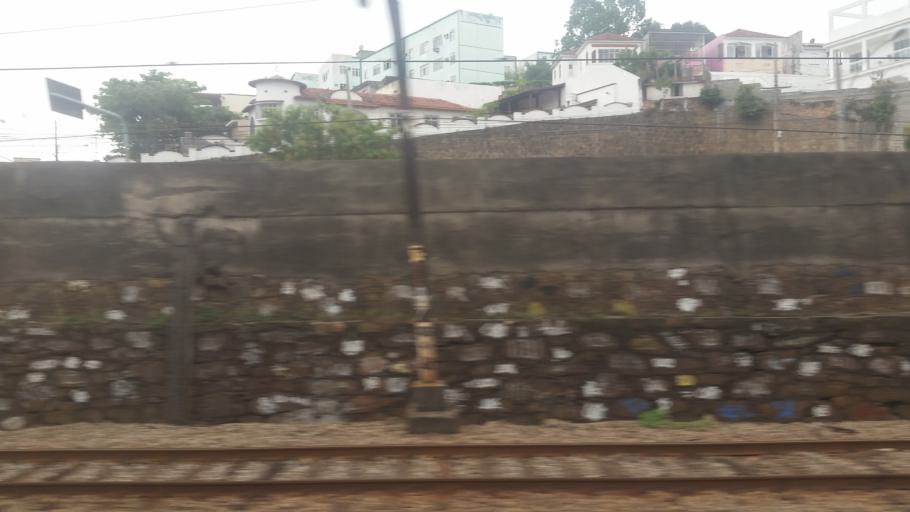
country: BR
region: Rio de Janeiro
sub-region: Rio De Janeiro
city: Rio de Janeiro
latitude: -22.8971
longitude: -43.2859
